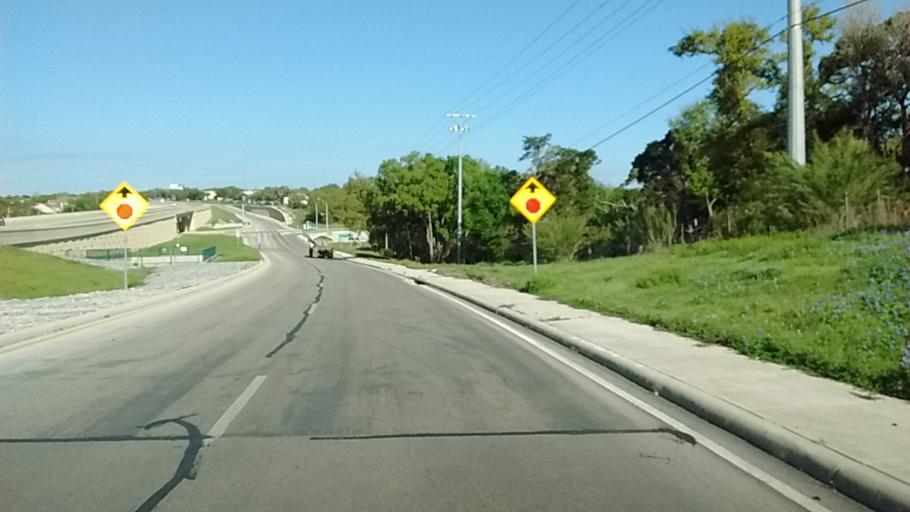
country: US
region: Texas
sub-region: Comal County
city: New Braunfels
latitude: 29.7372
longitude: -98.2009
